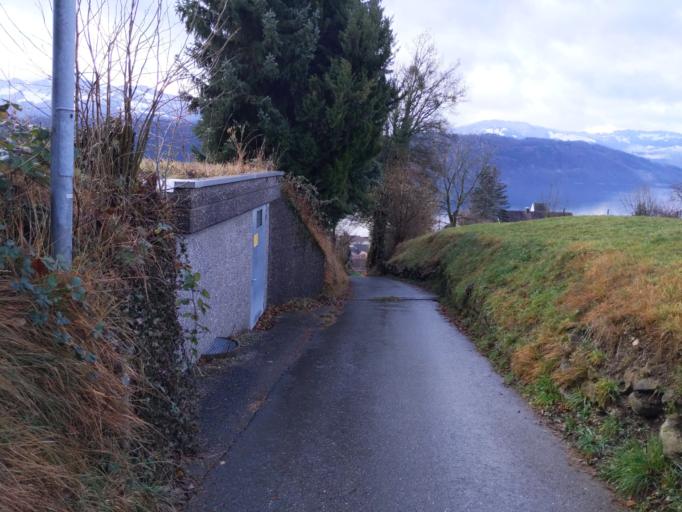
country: CH
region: Saint Gallen
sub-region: Wahlkreis See-Gaster
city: Schmerikon
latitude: 47.2284
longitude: 8.9428
